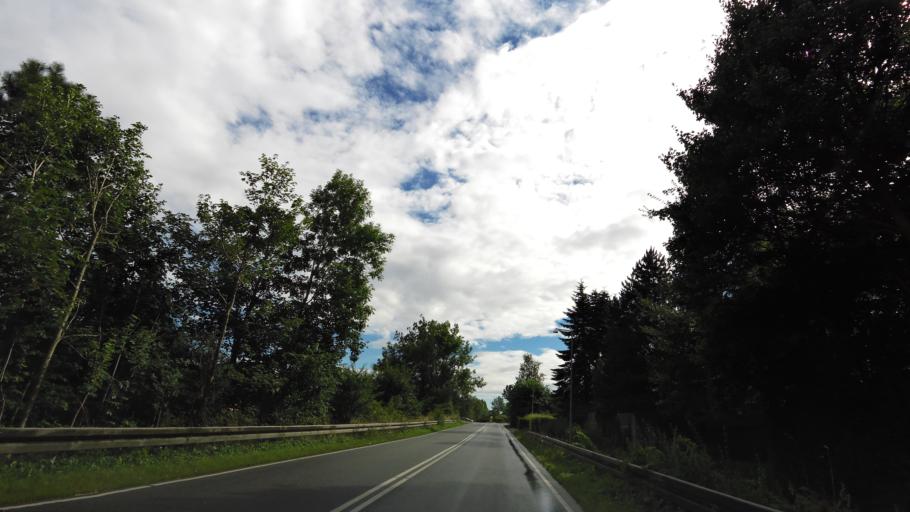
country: DK
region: South Denmark
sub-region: Assens Kommune
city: Vissenbjerg
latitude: 55.4444
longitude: 10.1838
